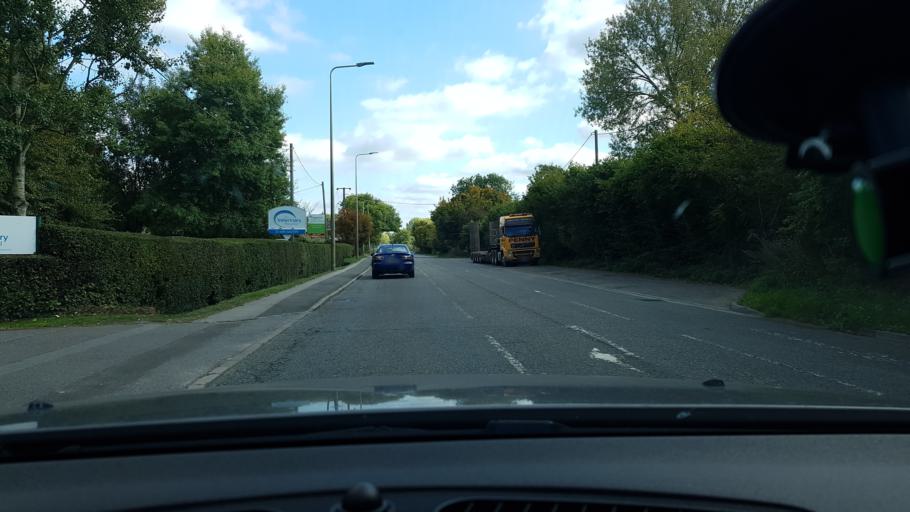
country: GB
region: England
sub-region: West Berkshire
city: Hungerford
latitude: 51.4180
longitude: -1.5058
